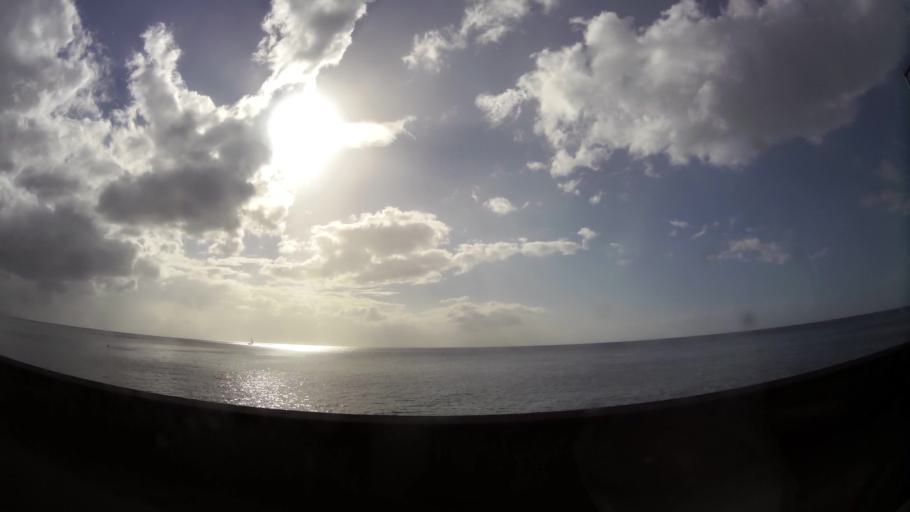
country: DM
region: Saint George
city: Roseau
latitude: 15.3224
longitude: -61.3949
